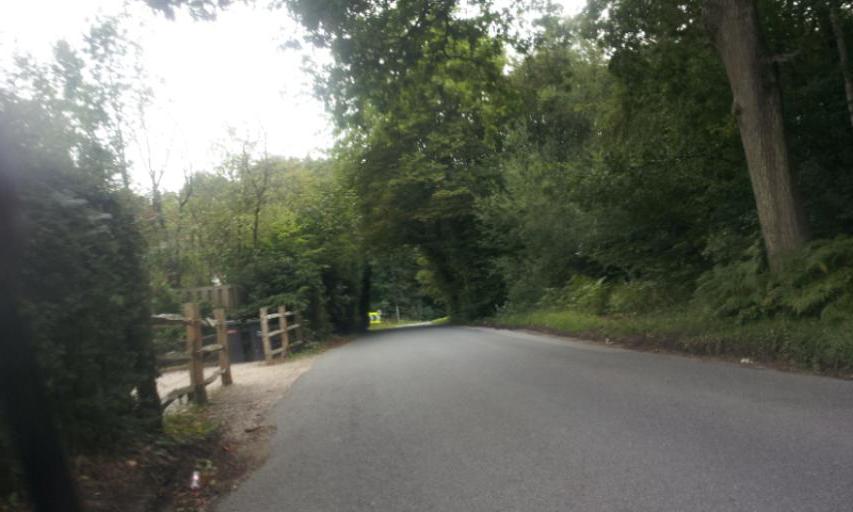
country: GB
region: England
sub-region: Kent
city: Tonbridge
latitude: 51.2299
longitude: 0.2939
